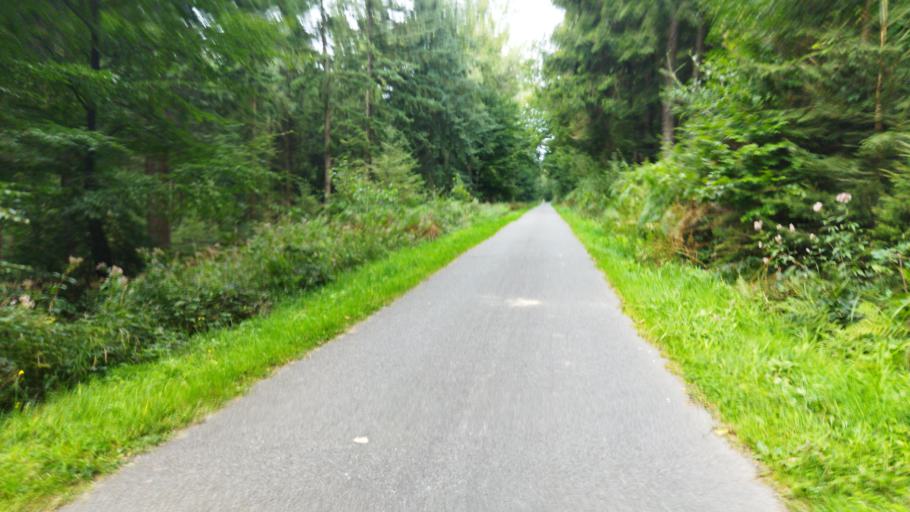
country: DE
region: Lower Saxony
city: Hilter
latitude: 52.1616
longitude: 8.1131
